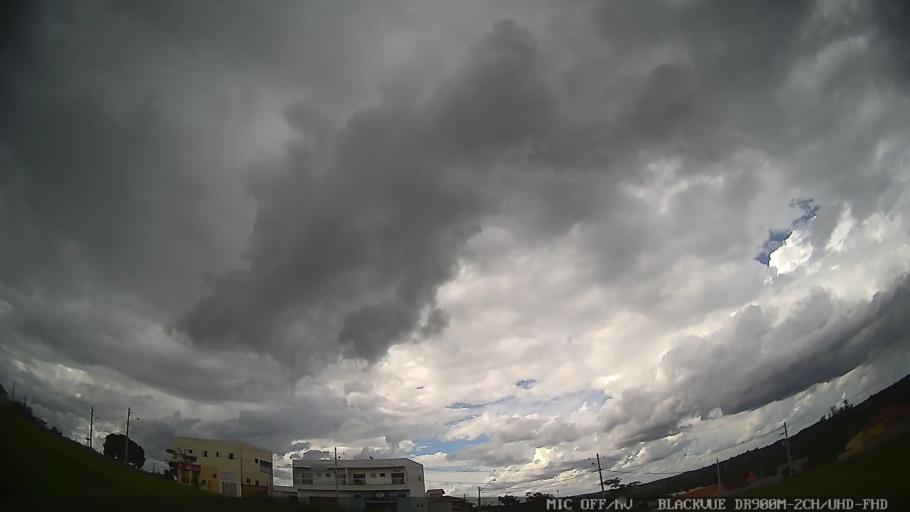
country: BR
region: Sao Paulo
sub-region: Jaguariuna
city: Jaguariuna
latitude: -22.6793
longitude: -46.9900
